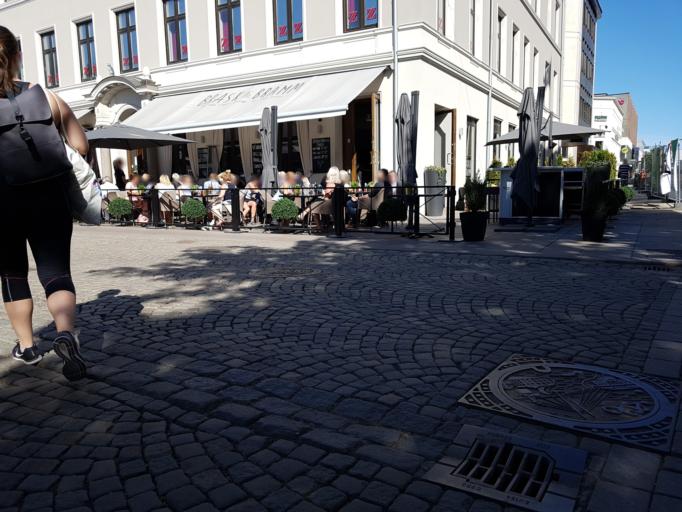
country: NO
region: Buskerud
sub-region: Drammen
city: Drammen
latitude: 59.7441
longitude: 10.2048
